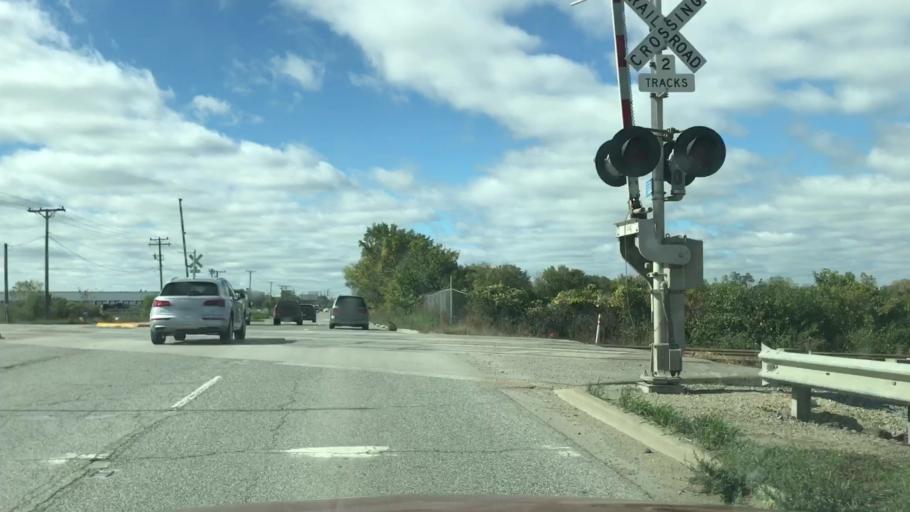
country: US
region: Illinois
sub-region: Cook County
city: Rosemont
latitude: 42.0085
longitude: -87.9245
